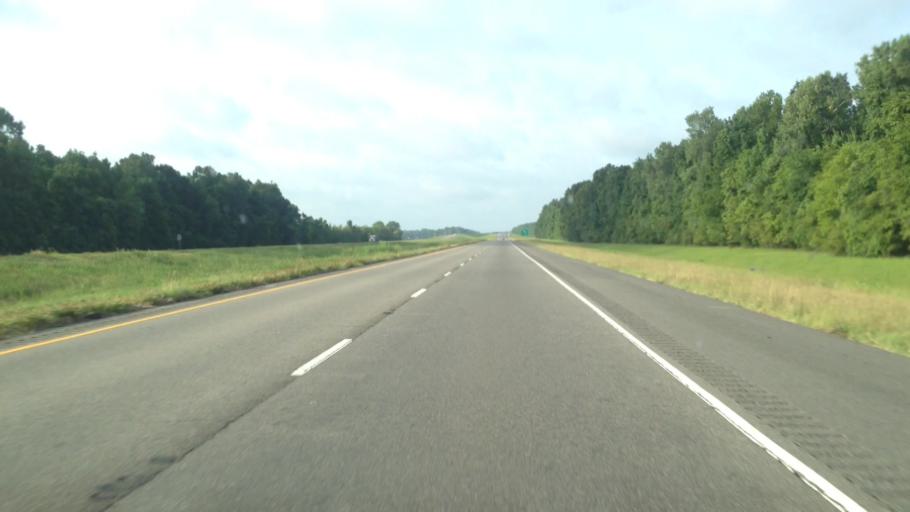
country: US
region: Louisiana
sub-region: Avoyelles Parish
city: Bunkie
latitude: 30.8771
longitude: -92.2278
